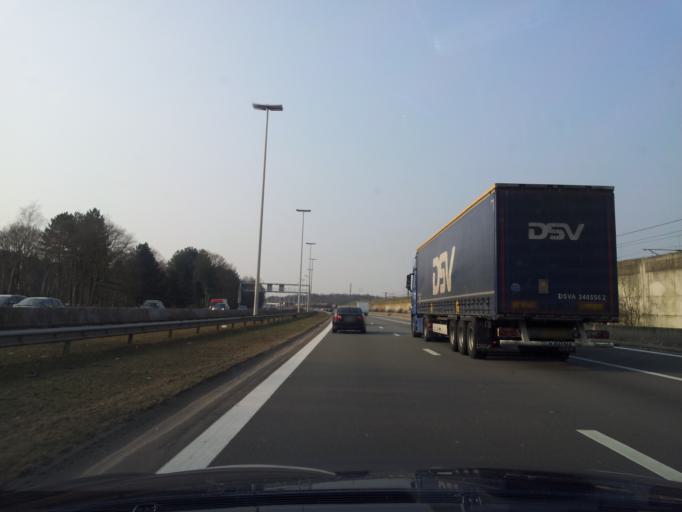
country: BE
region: Flanders
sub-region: Provincie Antwerpen
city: Brasschaat
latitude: 51.2900
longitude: 4.5191
